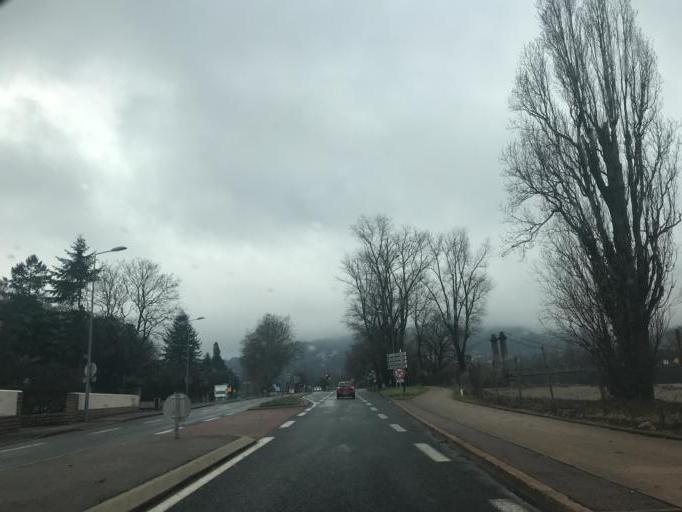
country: FR
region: Rhone-Alpes
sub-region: Departement du Rhone
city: Rochetaillee-sur-Saone
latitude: 45.8461
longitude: 4.8356
